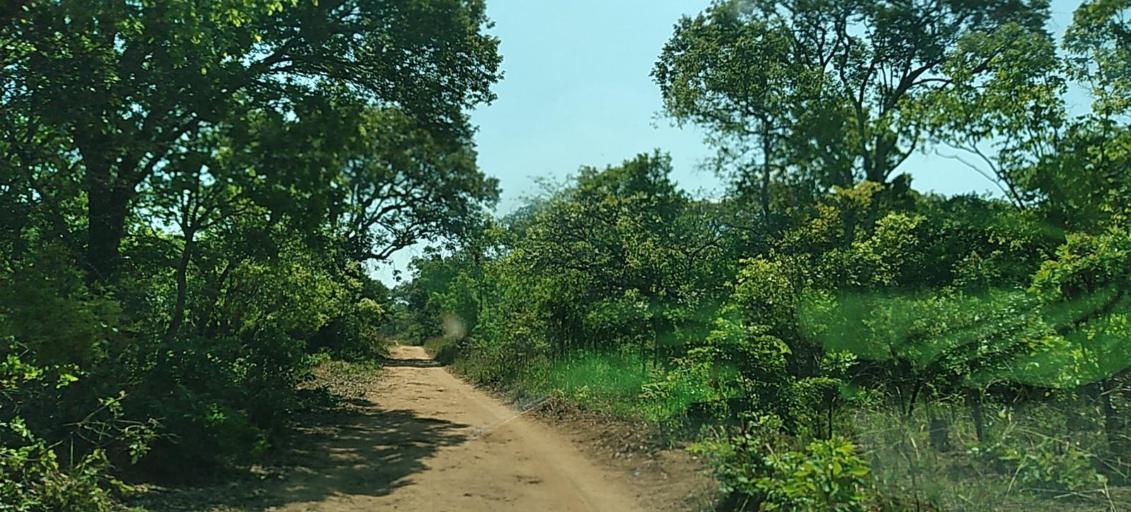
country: CD
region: Katanga
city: Kolwezi
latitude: -11.2790
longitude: 25.1332
